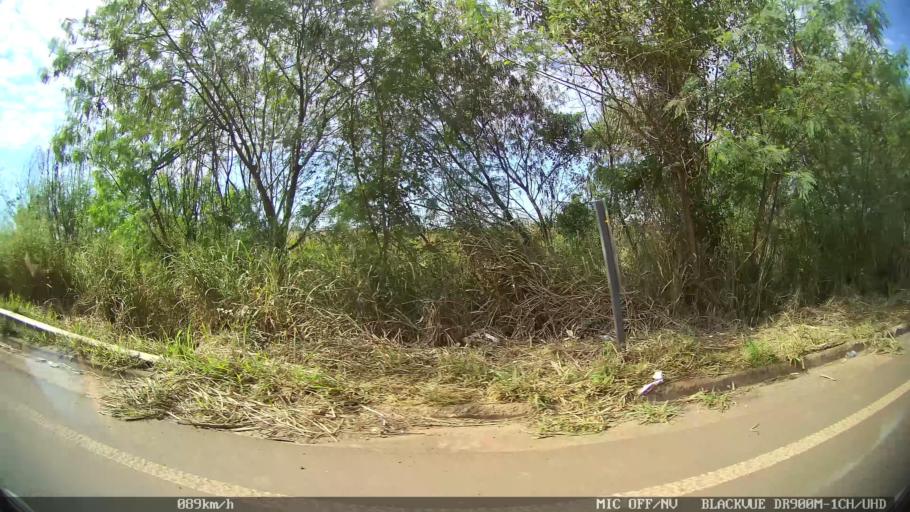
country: BR
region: Sao Paulo
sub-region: Santa Barbara D'Oeste
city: Santa Barbara d'Oeste
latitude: -22.7337
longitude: -47.4239
